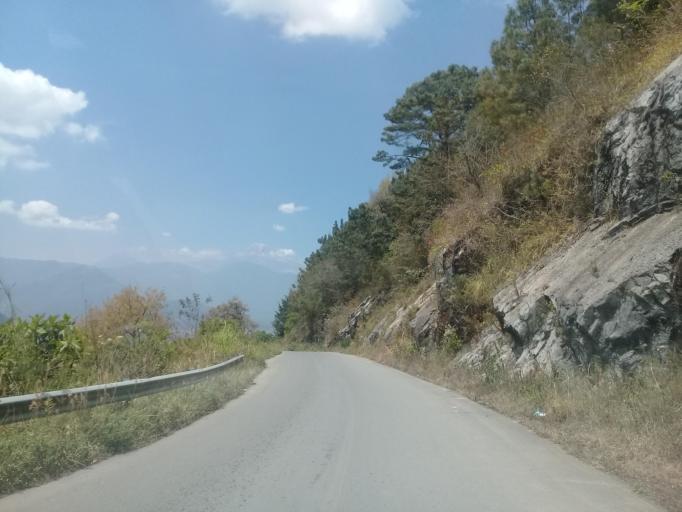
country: MX
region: Veracruz
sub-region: Tlilapan
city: Tonalixco
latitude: 18.7995
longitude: -97.0573
